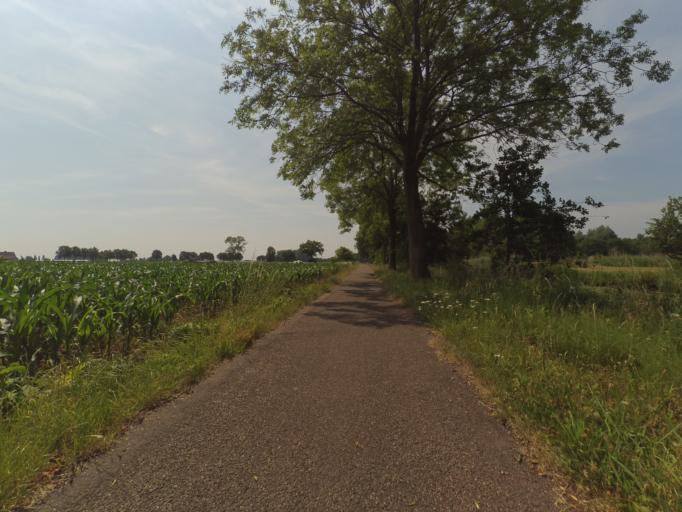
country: BE
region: Flanders
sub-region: Provincie Antwerpen
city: Hoogstraten
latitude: 51.4741
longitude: 4.7539
